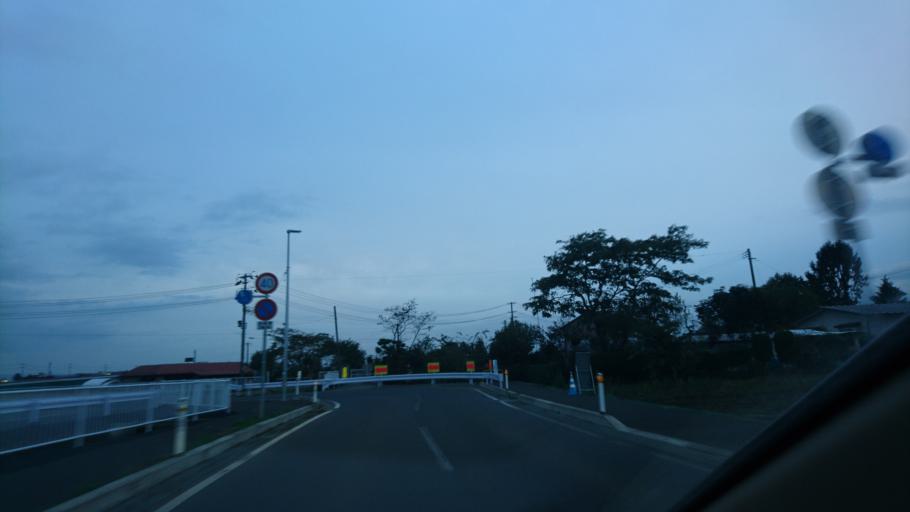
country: JP
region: Iwate
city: Morioka-shi
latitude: 39.6685
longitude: 141.1329
